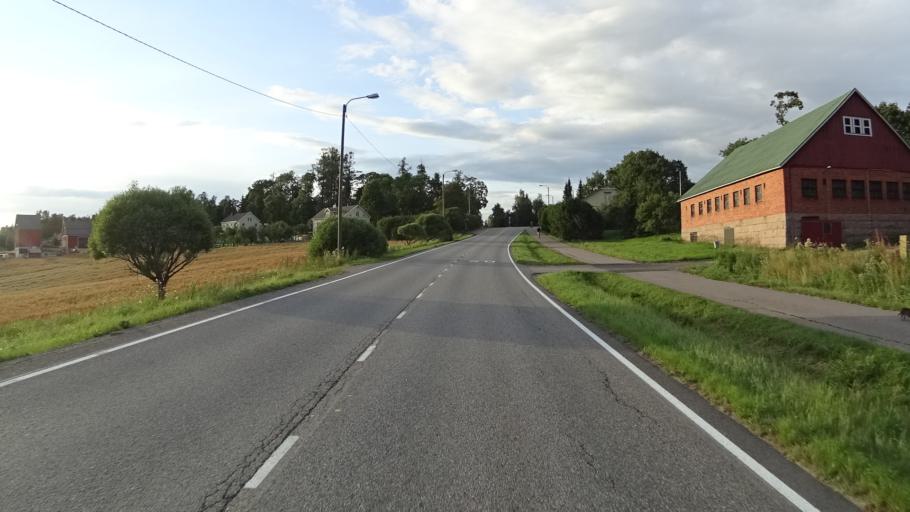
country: FI
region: Uusimaa
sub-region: Helsinki
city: Nurmijaervi
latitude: 60.3463
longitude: 24.8659
